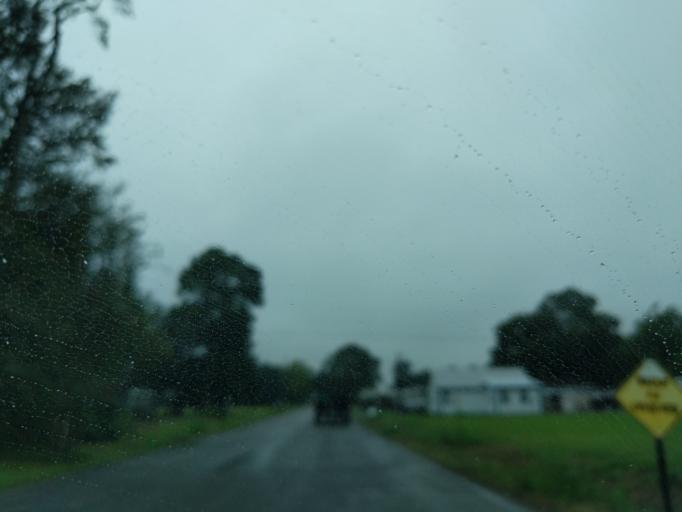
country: US
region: Louisiana
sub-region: Vermilion Parish
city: Kaplan
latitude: 29.9938
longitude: -92.2824
